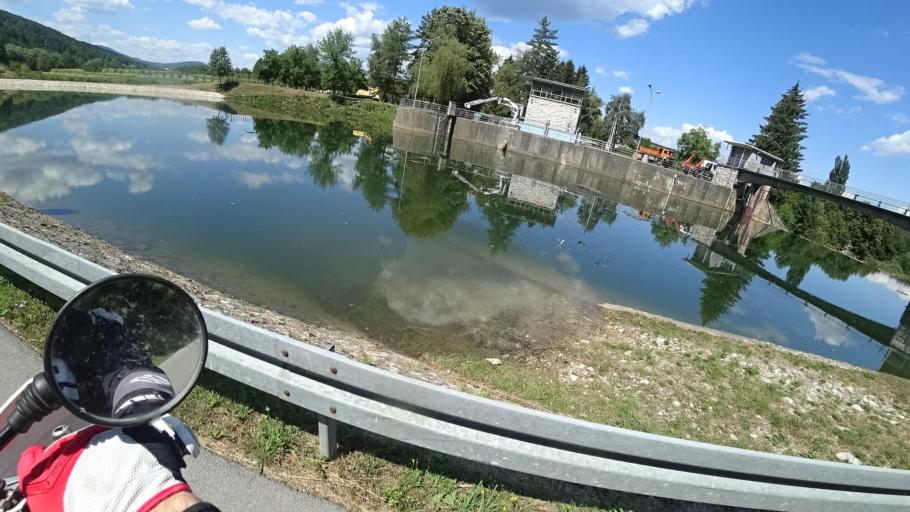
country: HR
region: Karlovacka
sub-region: Grad Ogulin
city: Ogulin
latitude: 45.2530
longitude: 15.2142
